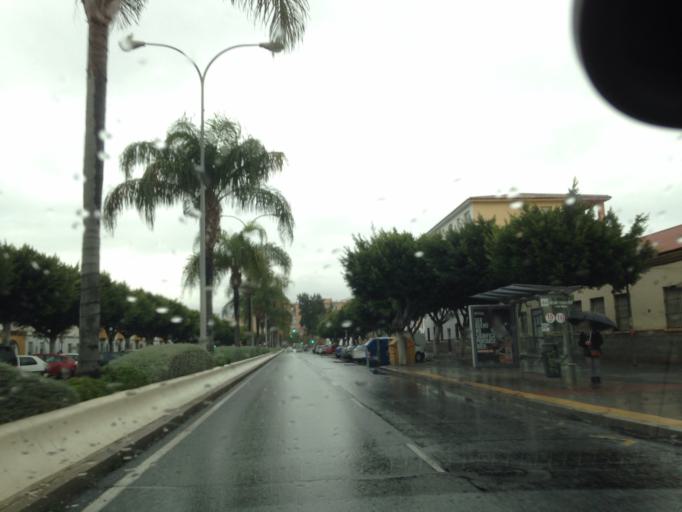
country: ES
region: Andalusia
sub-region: Provincia de Malaga
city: Malaga
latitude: 36.6973
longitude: -4.4415
